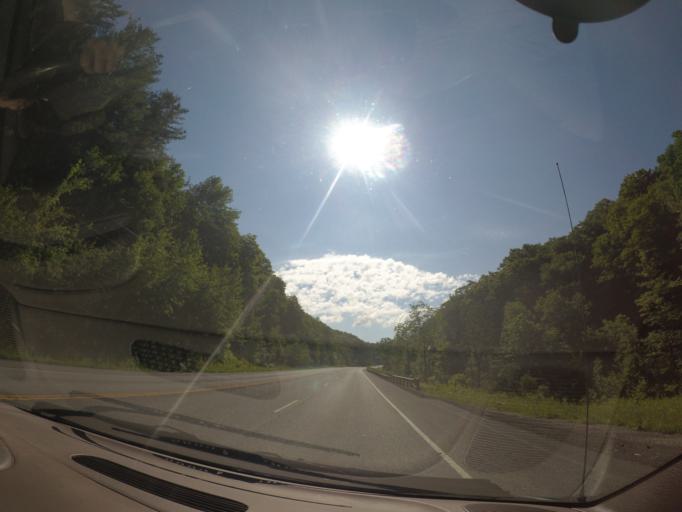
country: US
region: Vermont
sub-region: Bennington County
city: Bennington
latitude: 42.8786
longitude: -73.0979
